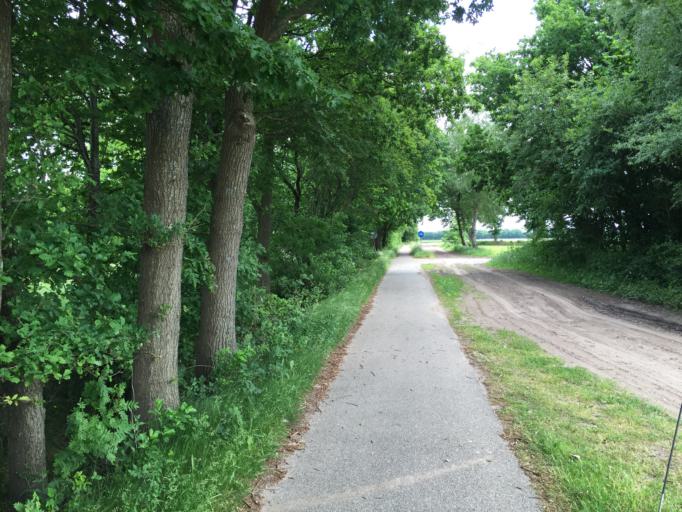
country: NL
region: Drenthe
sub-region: Gemeente Westerveld
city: Dwingeloo
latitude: 52.9076
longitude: 6.4705
